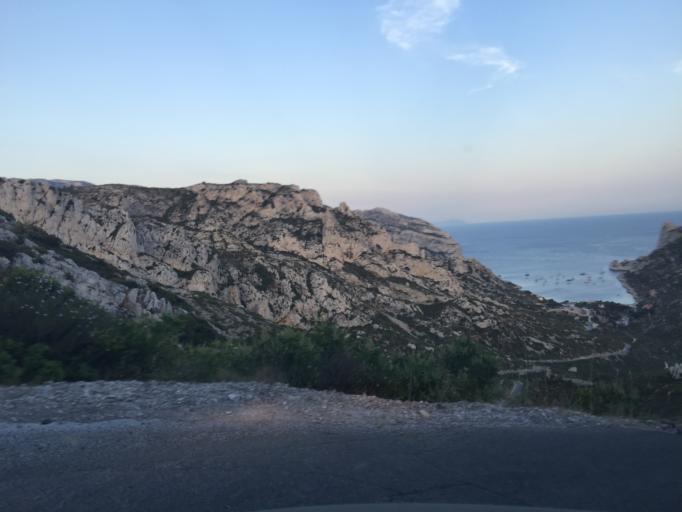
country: FR
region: Provence-Alpes-Cote d'Azur
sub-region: Departement des Bouches-du-Rhone
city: Marseille 09
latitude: 43.2164
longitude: 5.4103
